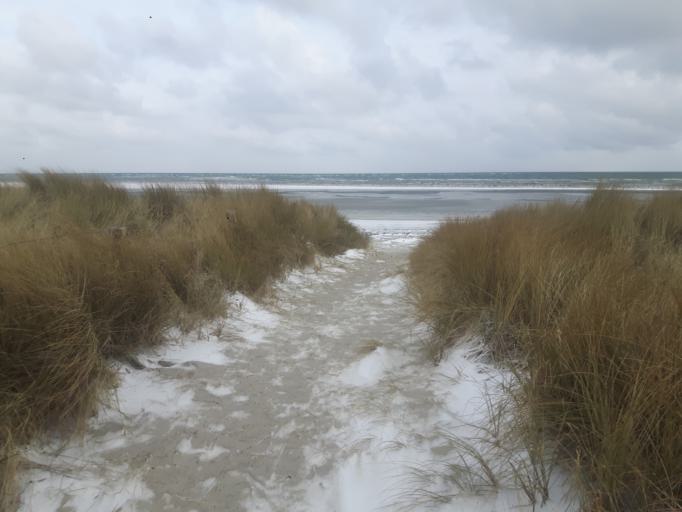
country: DE
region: Schleswig-Holstein
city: Fehmarn
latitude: 54.5093
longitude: 11.1946
